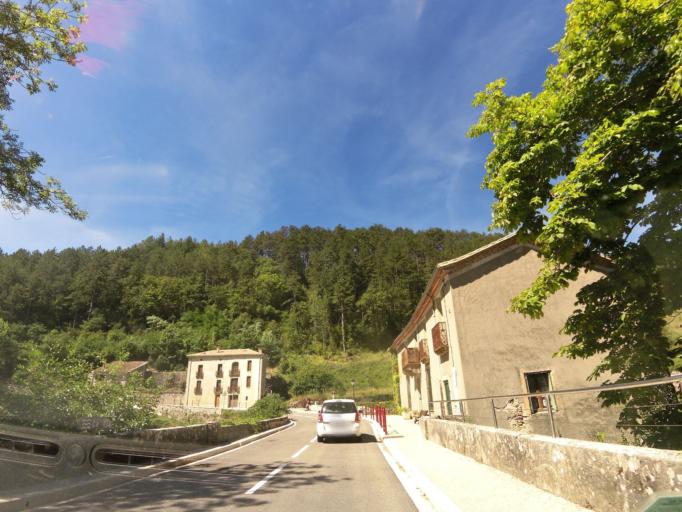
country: FR
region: Languedoc-Roussillon
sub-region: Departement du Gard
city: Le Vigan
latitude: 43.9659
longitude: 3.4379
